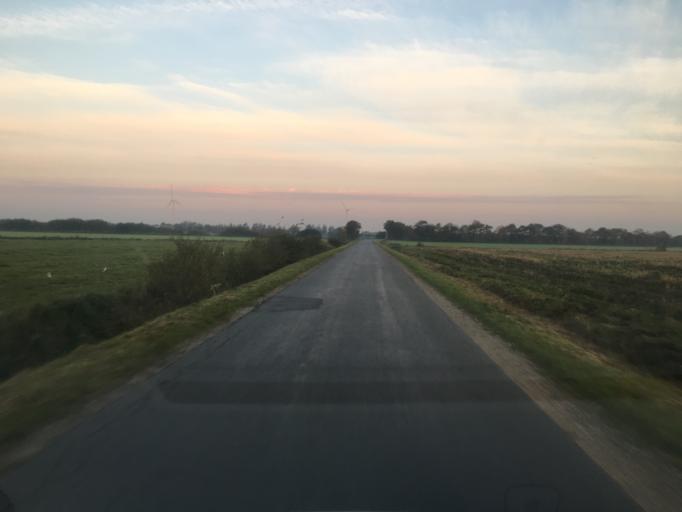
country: DK
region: South Denmark
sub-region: Tonder Kommune
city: Logumkloster
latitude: 54.9844
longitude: 9.0602
